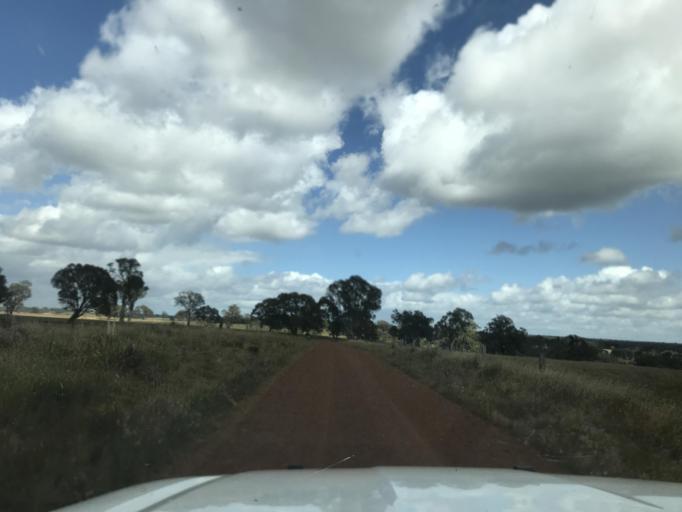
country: AU
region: South Australia
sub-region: Wattle Range
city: Penola
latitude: -37.1938
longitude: 141.4199
